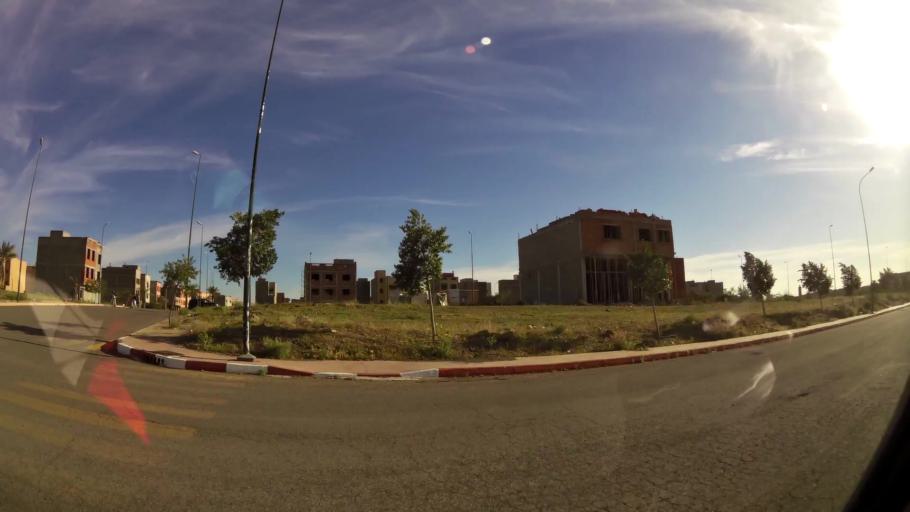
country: MA
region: Marrakech-Tensift-Al Haouz
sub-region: Marrakech
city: Marrakesh
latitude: 31.7542
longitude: -8.1055
